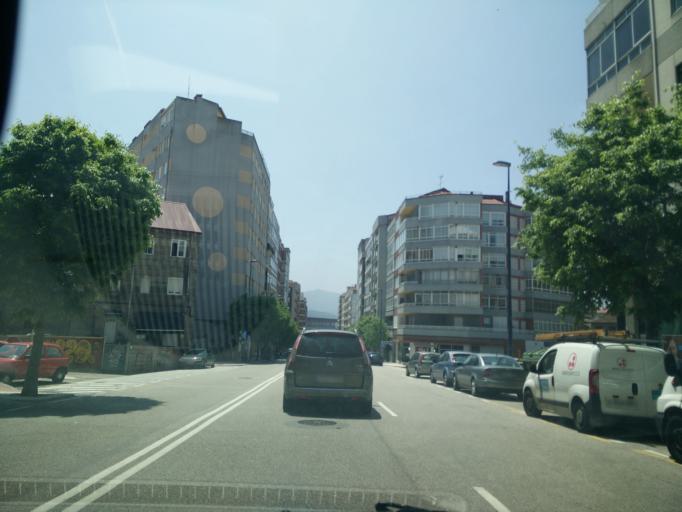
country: ES
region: Galicia
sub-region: Provincia de Pontevedra
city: Vigo
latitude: 42.2157
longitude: -8.7358
